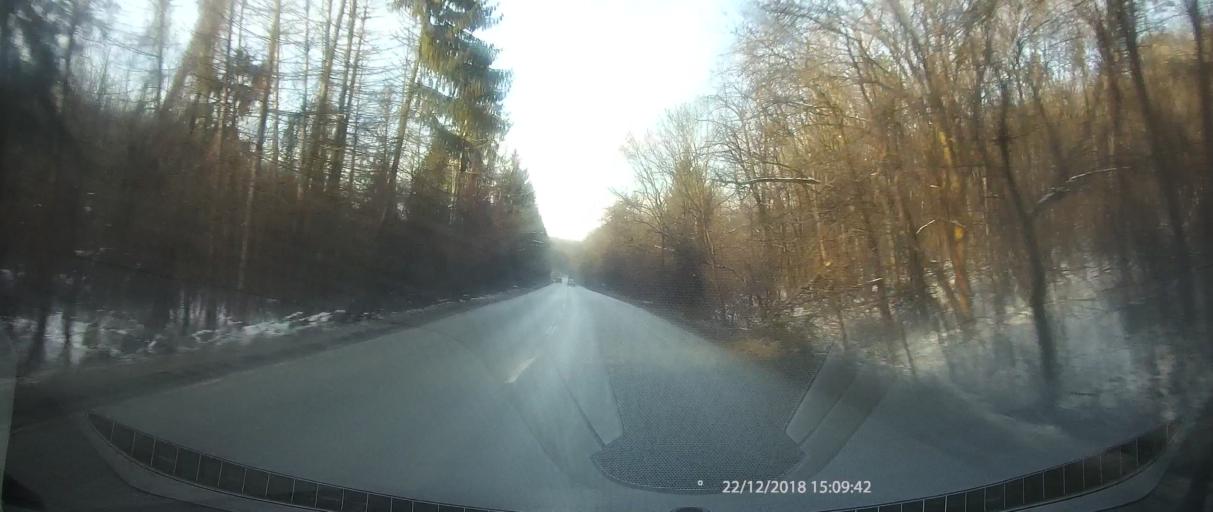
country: BG
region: Ruse
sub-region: Obshtina Borovo
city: Borovo
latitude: 43.5053
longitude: 25.7982
